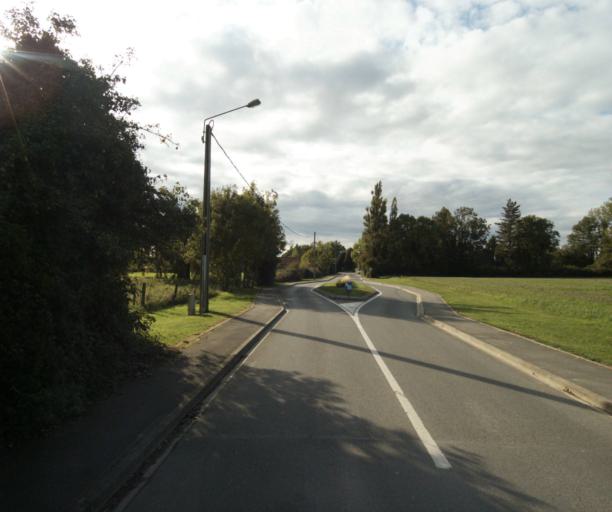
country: FR
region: Nord-Pas-de-Calais
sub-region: Departement du Nord
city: Ennetieres-en-Weppes
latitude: 50.6351
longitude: 2.9360
